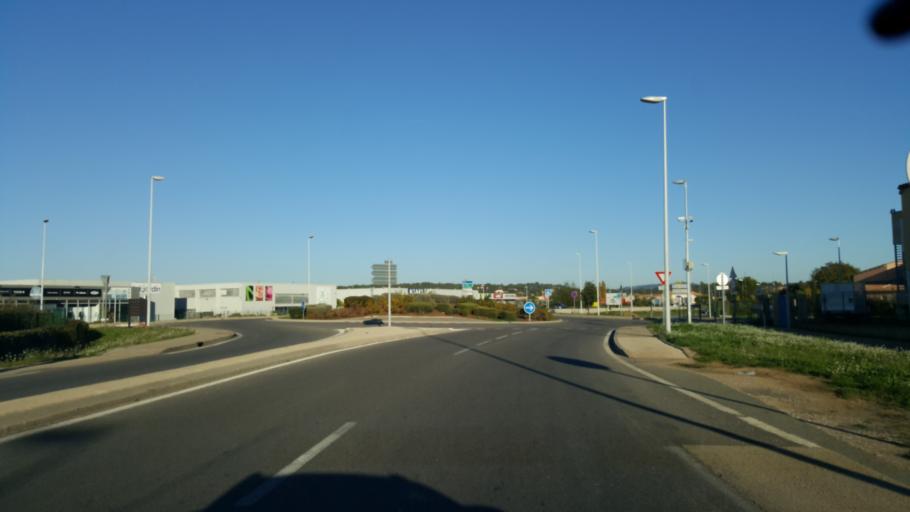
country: FR
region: Provence-Alpes-Cote d'Azur
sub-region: Departement du Var
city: Saint-Maximin-la-Sainte-Baume
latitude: 43.4585
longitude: 5.8591
